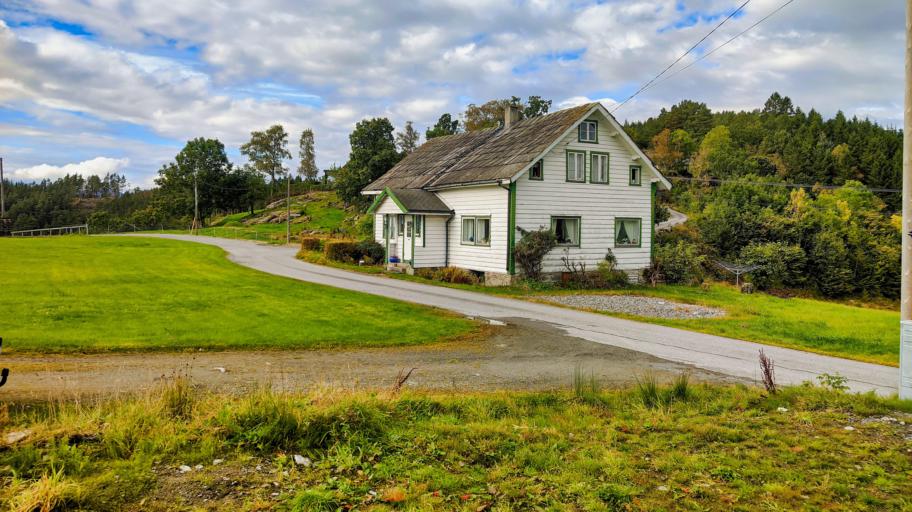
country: NO
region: Hordaland
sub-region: Stord
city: Leirvik
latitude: 59.8362
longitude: 5.7014
